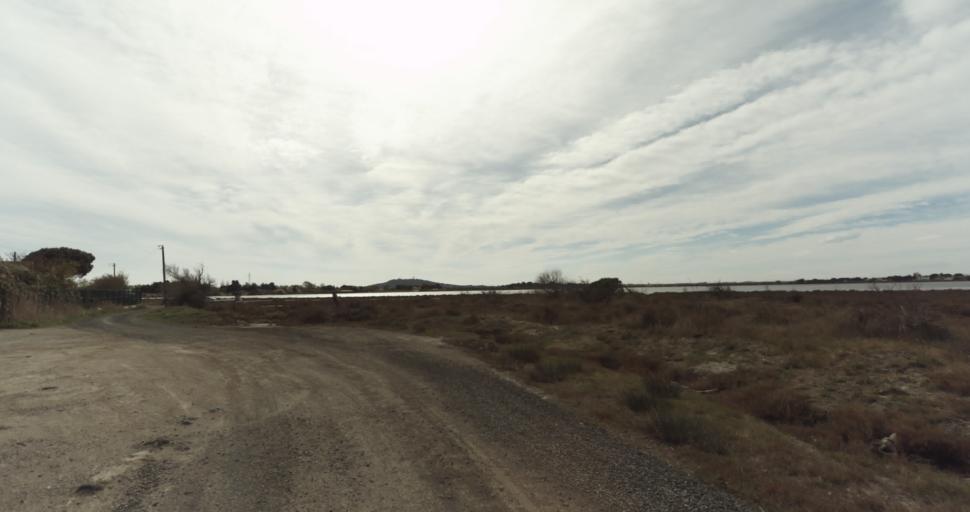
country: FR
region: Languedoc-Roussillon
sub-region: Departement de l'Herault
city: Marseillan
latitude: 43.3259
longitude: 3.5437
